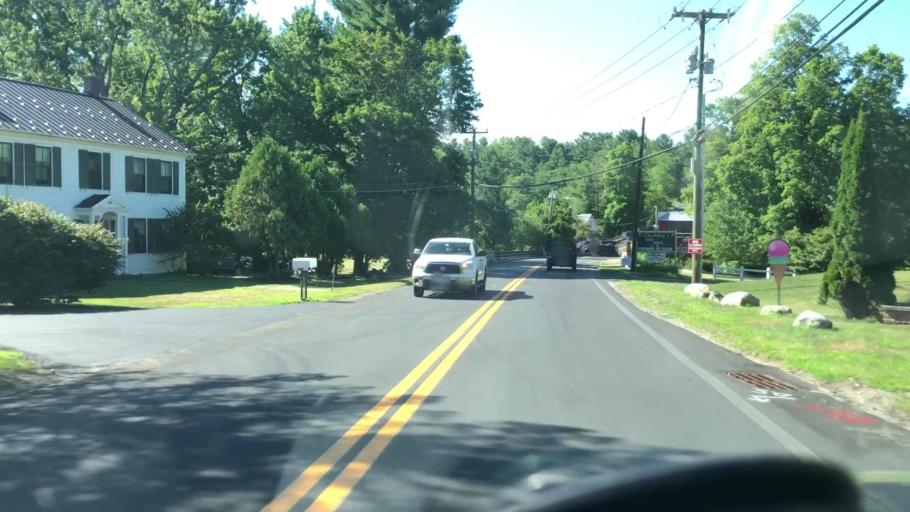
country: US
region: Massachusetts
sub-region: Hampshire County
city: Southampton
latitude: 42.2162
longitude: -72.7304
